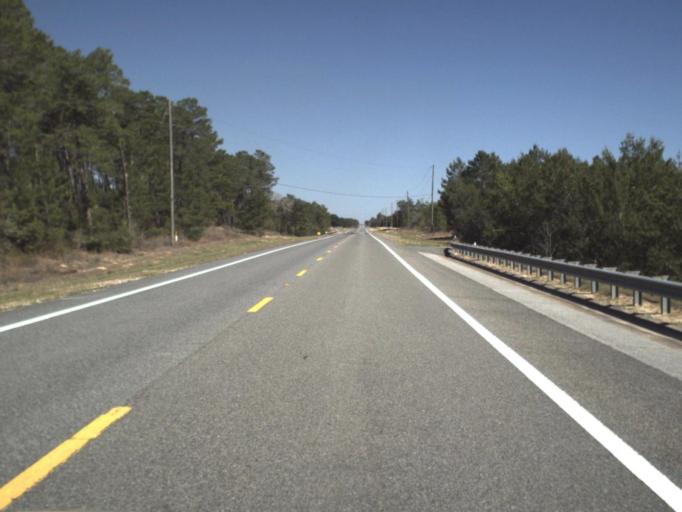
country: US
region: Florida
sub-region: Bay County
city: Lynn Haven
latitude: 30.4246
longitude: -85.6431
